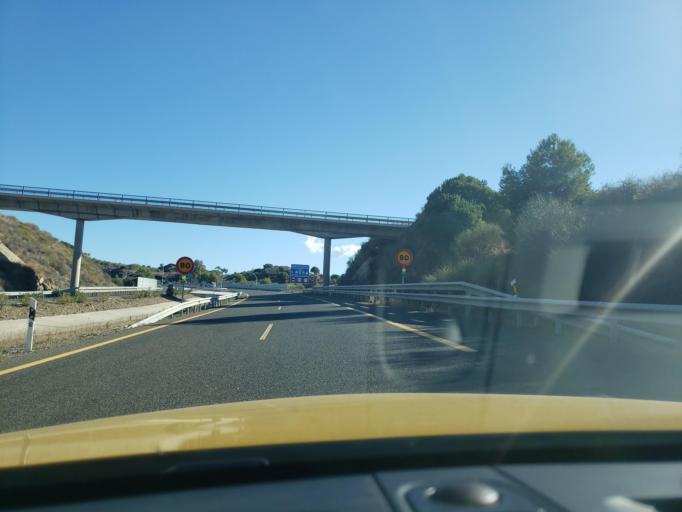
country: ES
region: Andalusia
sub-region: Provincia de Malaga
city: Fuengirola
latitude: 36.5038
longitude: -4.7353
